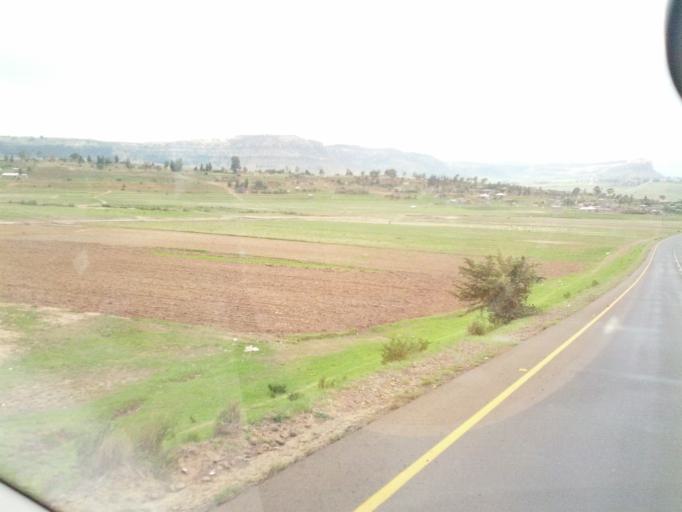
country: LS
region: Maseru
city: Maseru
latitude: -29.4147
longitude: 27.6344
